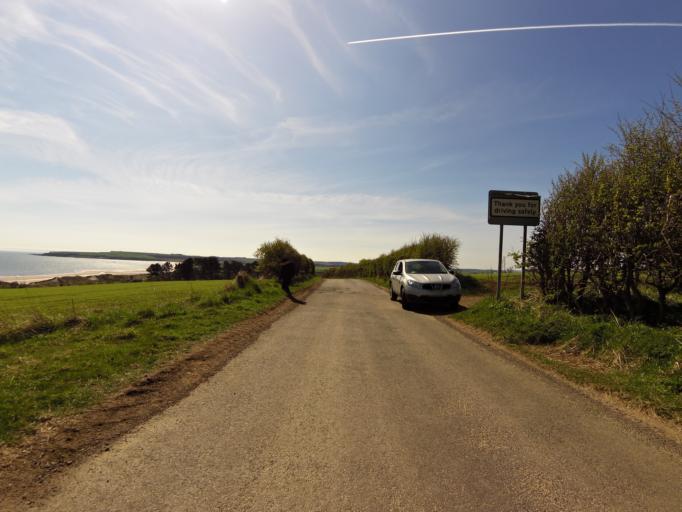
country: GB
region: Scotland
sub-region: Angus
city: Montrose
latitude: 56.6635
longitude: -2.5080
